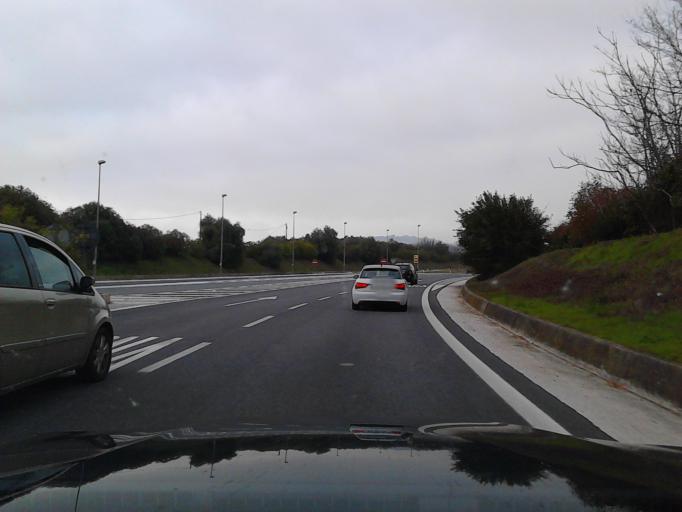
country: IT
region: Abruzzo
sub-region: Provincia di Teramo
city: Villa Rosa
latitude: 42.8366
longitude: 13.9012
